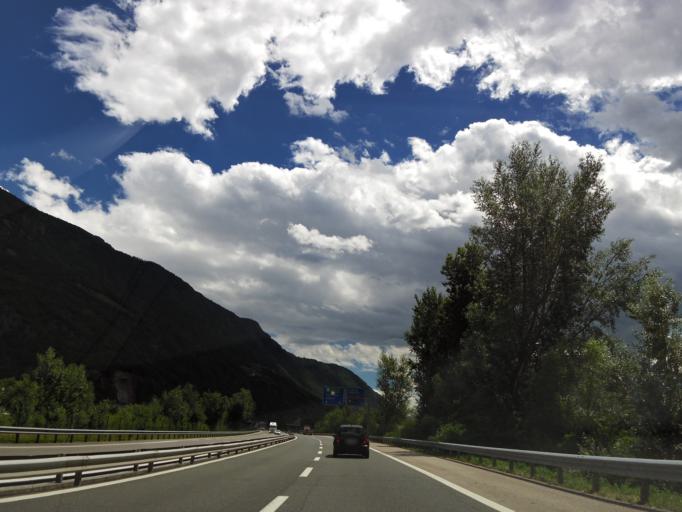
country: IT
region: Trentino-Alto Adige
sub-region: Bolzano
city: Sinigo
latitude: 46.6336
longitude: 11.1726
